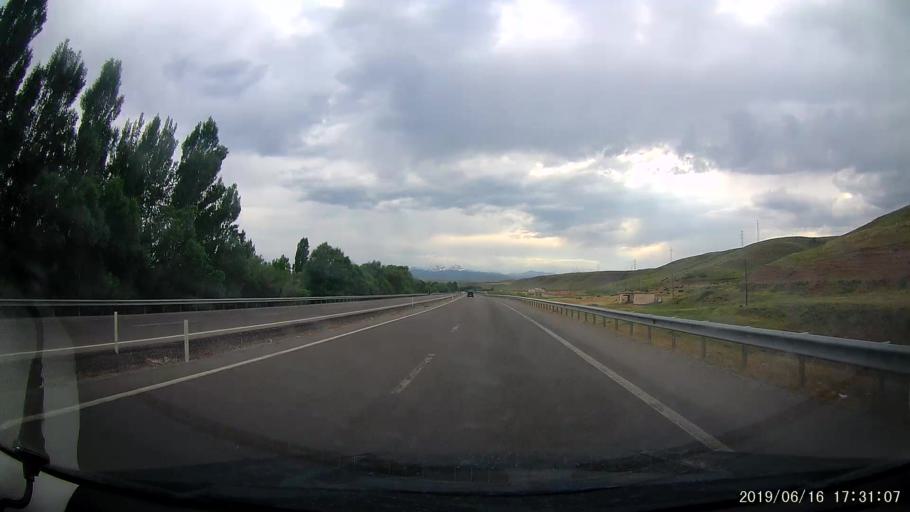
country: TR
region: Erzincan
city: Tercan
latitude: 39.7747
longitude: 40.3310
